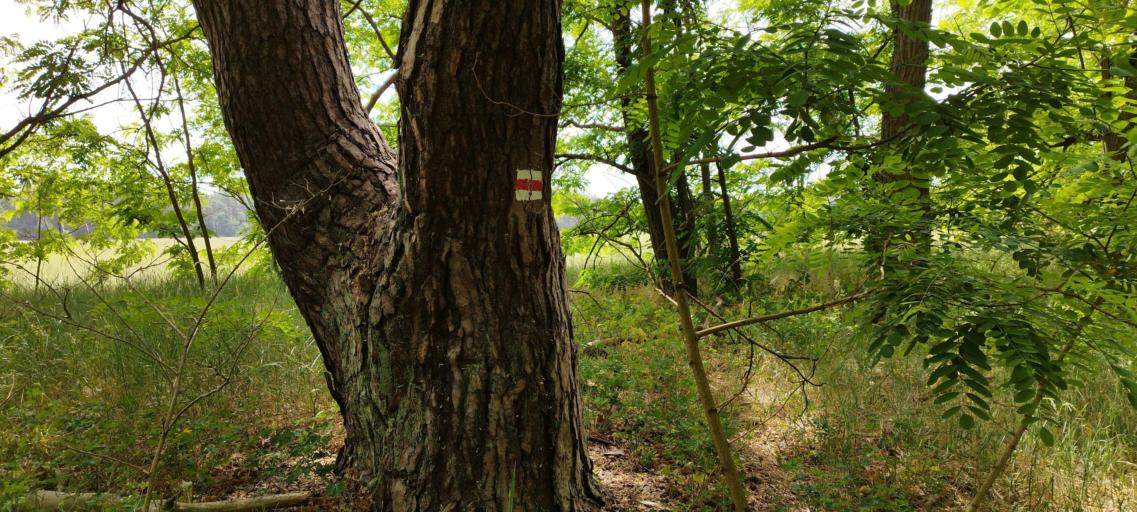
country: DE
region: Brandenburg
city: Rehfelde
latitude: 52.4528
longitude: 13.8997
